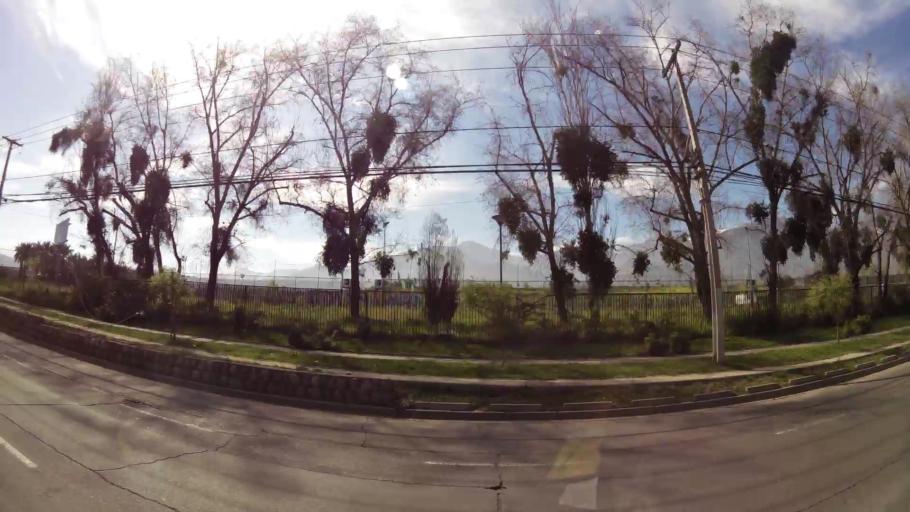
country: CL
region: Santiago Metropolitan
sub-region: Provincia de Santiago
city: Villa Presidente Frei, Nunoa, Santiago, Chile
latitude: -33.4297
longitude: -70.5392
